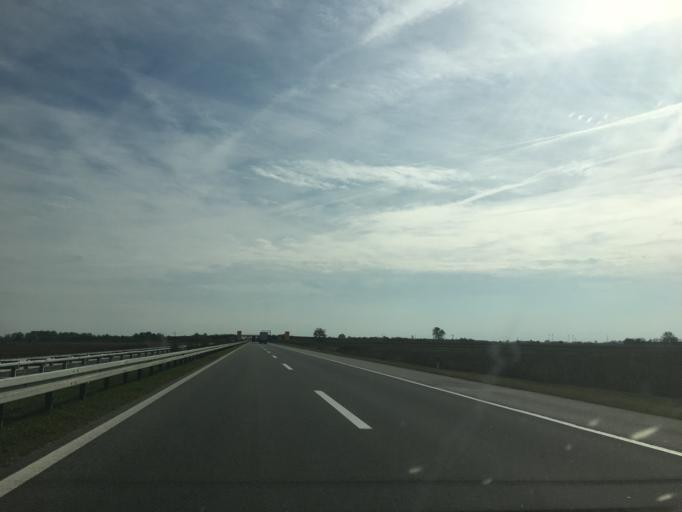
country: RS
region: Autonomna Pokrajina Vojvodina
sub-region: Sremski Okrug
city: Stara Pazova
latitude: 45.0165
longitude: 20.1956
